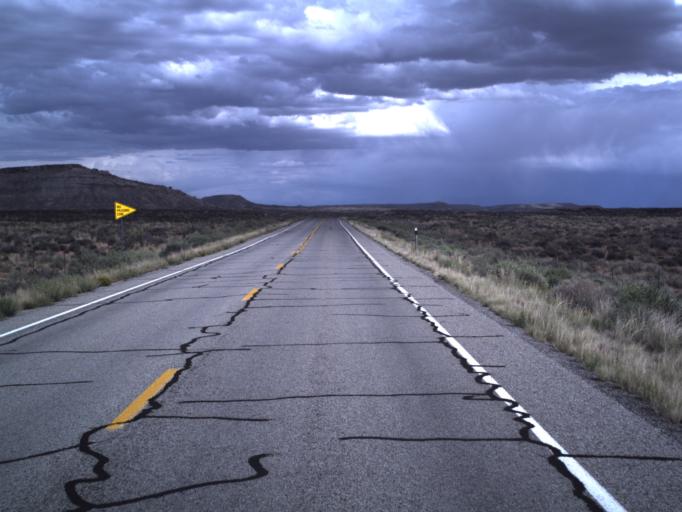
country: US
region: Utah
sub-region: San Juan County
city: Blanding
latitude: 37.2975
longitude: -109.4738
